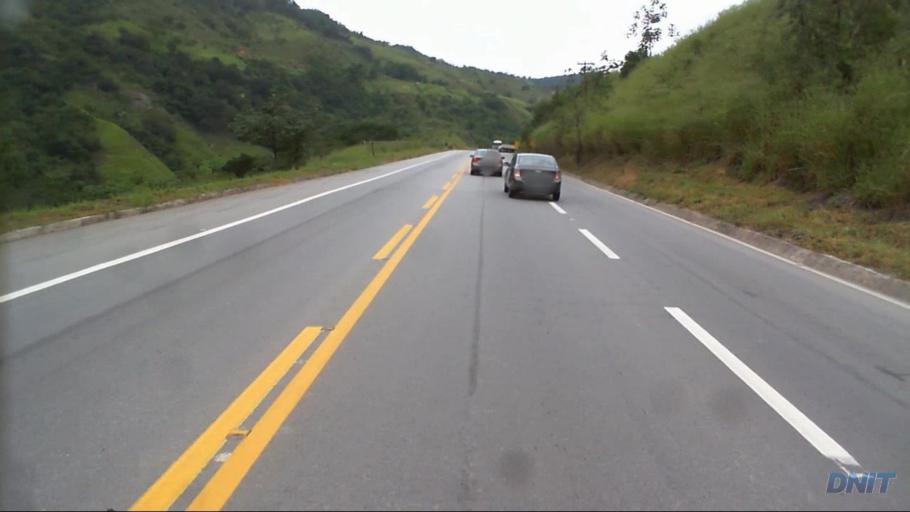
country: BR
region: Minas Gerais
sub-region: Timoteo
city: Timoteo
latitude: -19.6355
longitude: -42.8073
